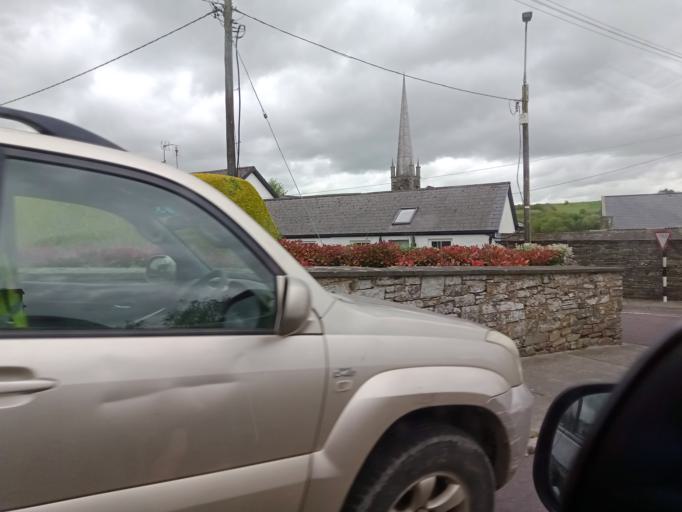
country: IE
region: Munster
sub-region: County Cork
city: Derry
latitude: 51.5774
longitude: -9.0309
